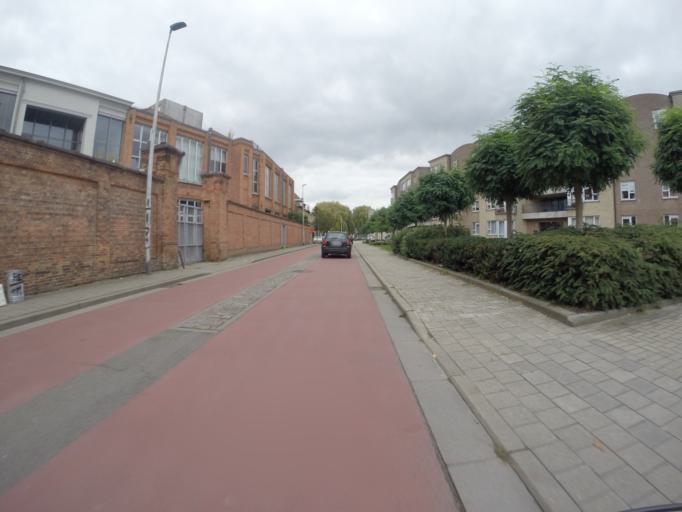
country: BE
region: Flanders
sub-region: Provincie Oost-Vlaanderen
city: Gent
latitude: 51.0634
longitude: 3.7183
